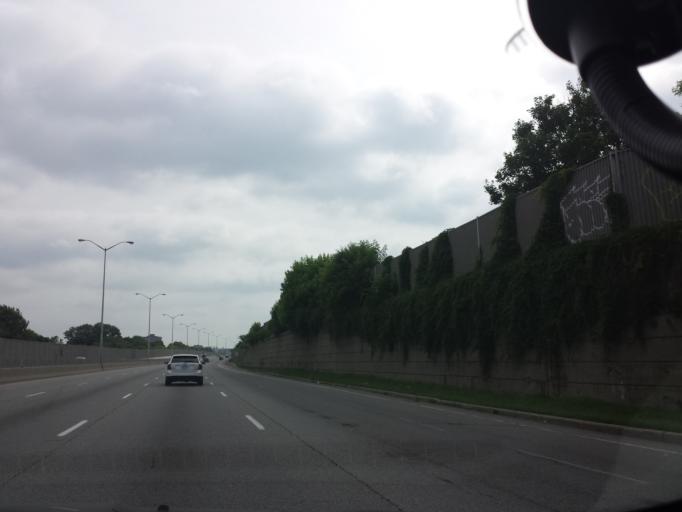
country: CA
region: Ontario
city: Ottawa
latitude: 45.3989
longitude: -75.7232
